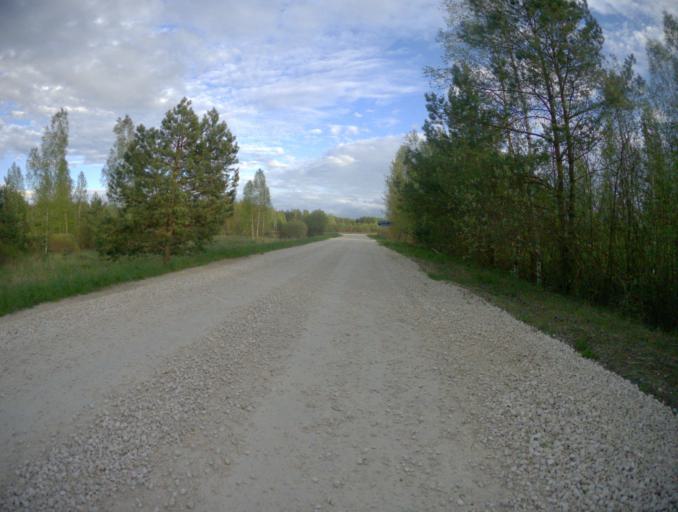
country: RU
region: Vladimir
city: Anopino
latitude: 55.7091
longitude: 40.6285
